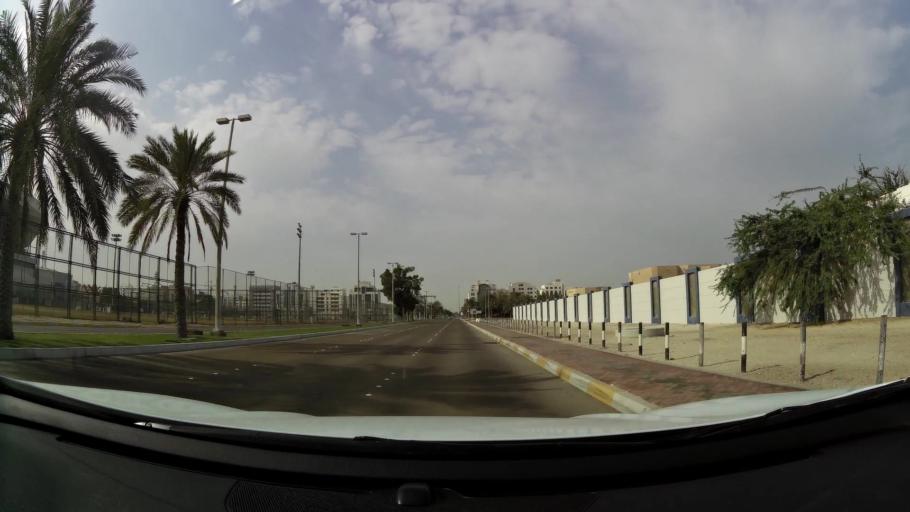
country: AE
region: Abu Dhabi
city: Abu Dhabi
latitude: 24.4548
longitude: 54.3908
